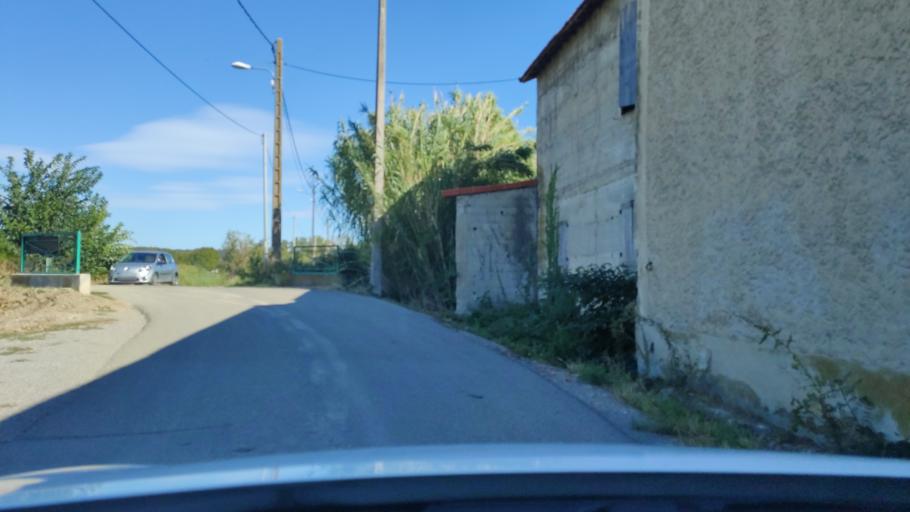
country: FR
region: Provence-Alpes-Cote d'Azur
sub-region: Departement du Vaucluse
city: Morieres-les-Avignon
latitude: 43.9280
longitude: 4.8895
